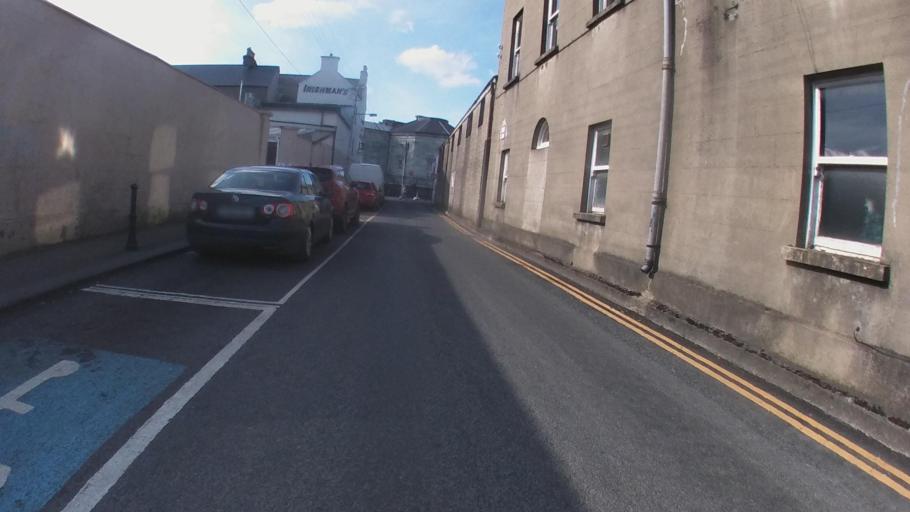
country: IE
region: Leinster
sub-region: County Carlow
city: Carlow
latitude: 52.8382
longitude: -6.9296
